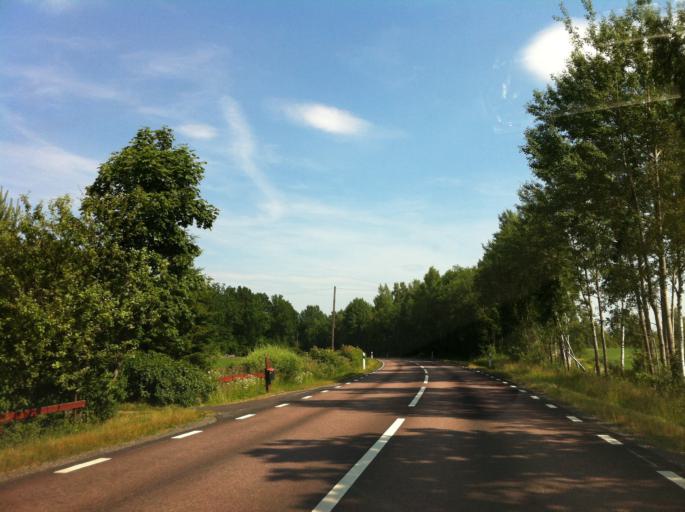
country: SE
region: Kalmar
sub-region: Nybro Kommun
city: Nybro
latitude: 56.7834
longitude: 15.8129
